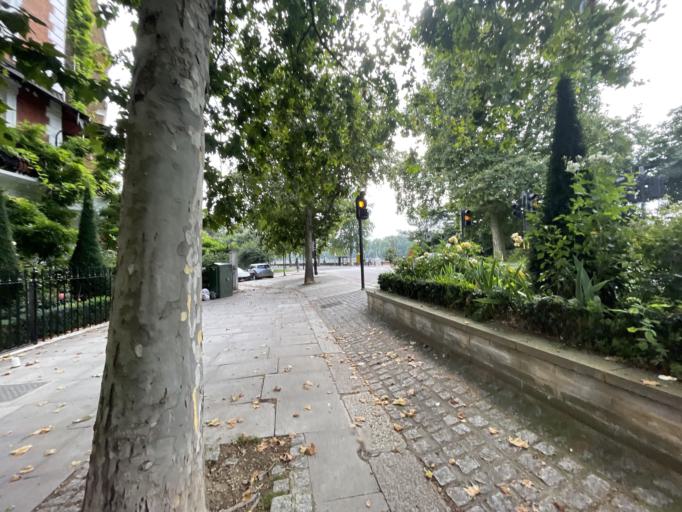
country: GB
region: England
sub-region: Greater London
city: Chelsea
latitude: 51.4836
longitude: -0.1671
